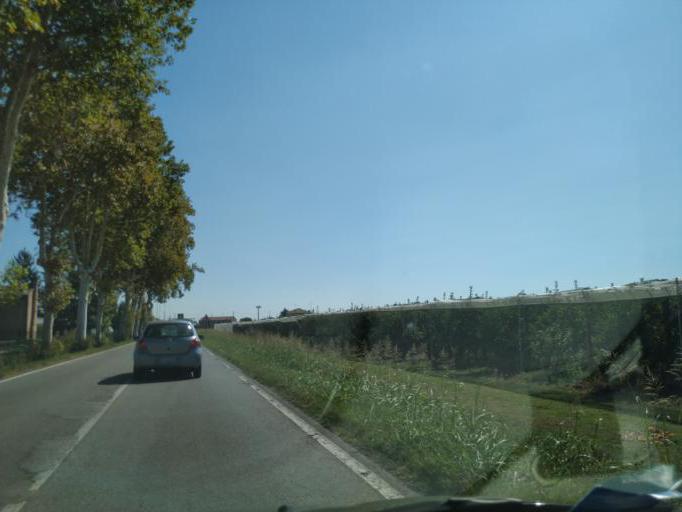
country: IT
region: Emilia-Romagna
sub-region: Provincia di Ferrara
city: La Saletta-Tamara
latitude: 44.8808
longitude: 11.7550
